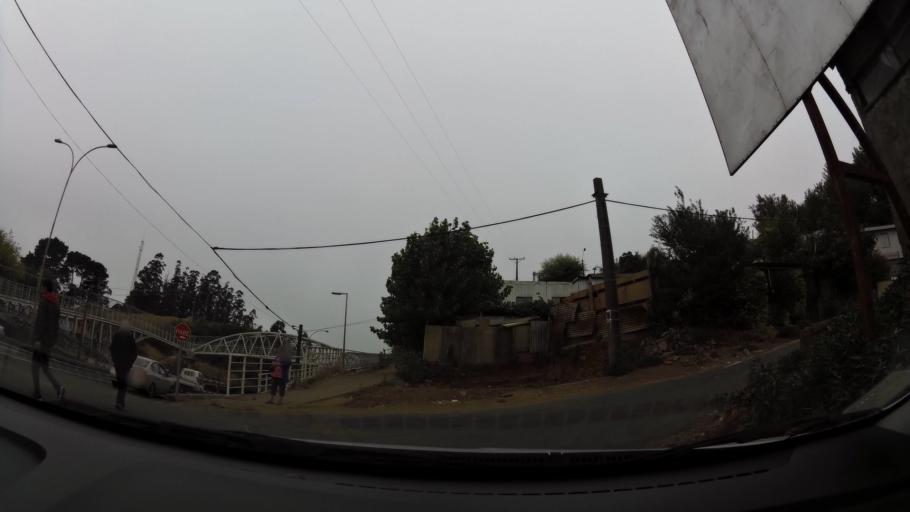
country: CL
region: Biobio
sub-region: Provincia de Concepcion
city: Concepcion
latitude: -36.8068
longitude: -73.0356
